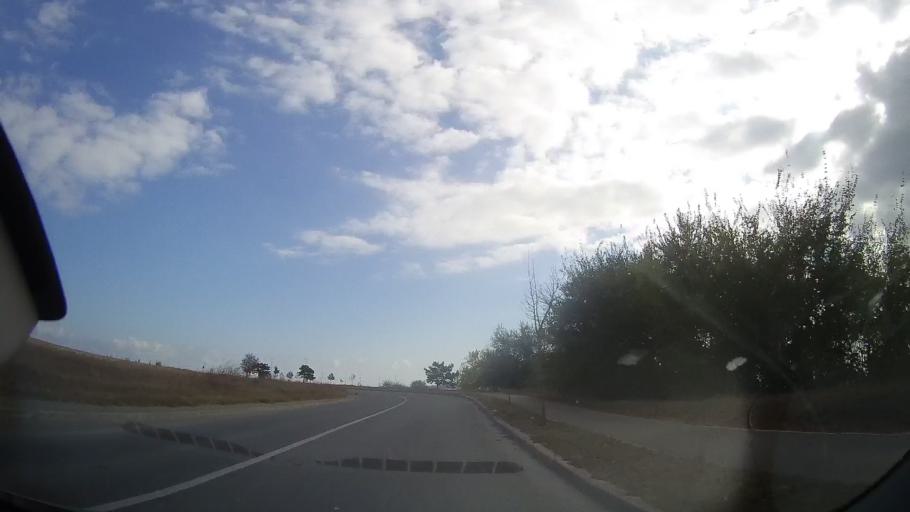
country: RO
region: Constanta
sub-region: Oras Techirghiol
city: Techirghiol
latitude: 44.0576
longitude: 28.6111
